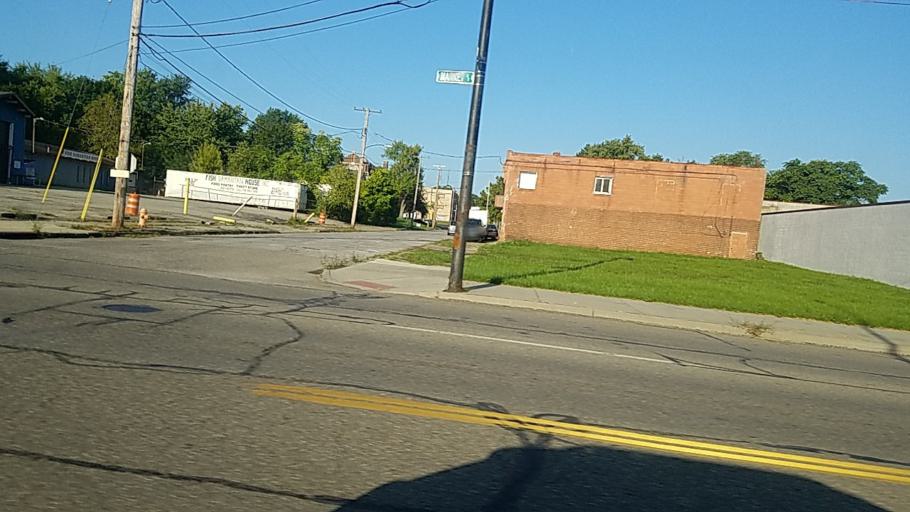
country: US
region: Ohio
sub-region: Mahoning County
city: Youngstown
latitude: 41.0868
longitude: -80.6568
